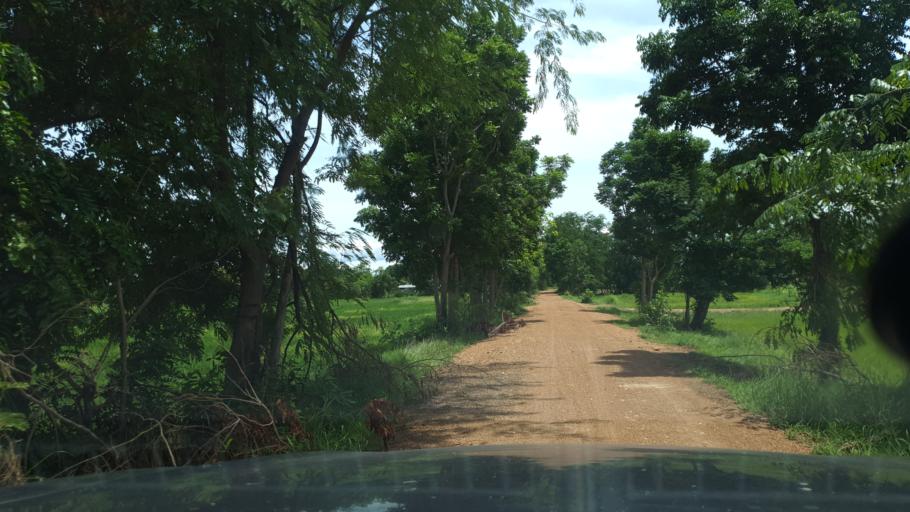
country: TH
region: Sukhothai
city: Ban Na
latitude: 17.0723
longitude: 99.6974
